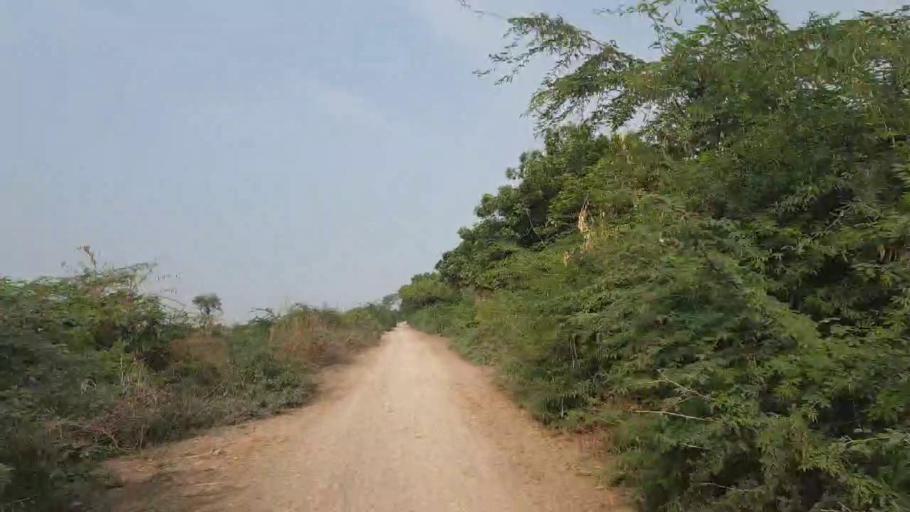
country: PK
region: Sindh
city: Badin
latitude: 24.5957
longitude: 68.7413
